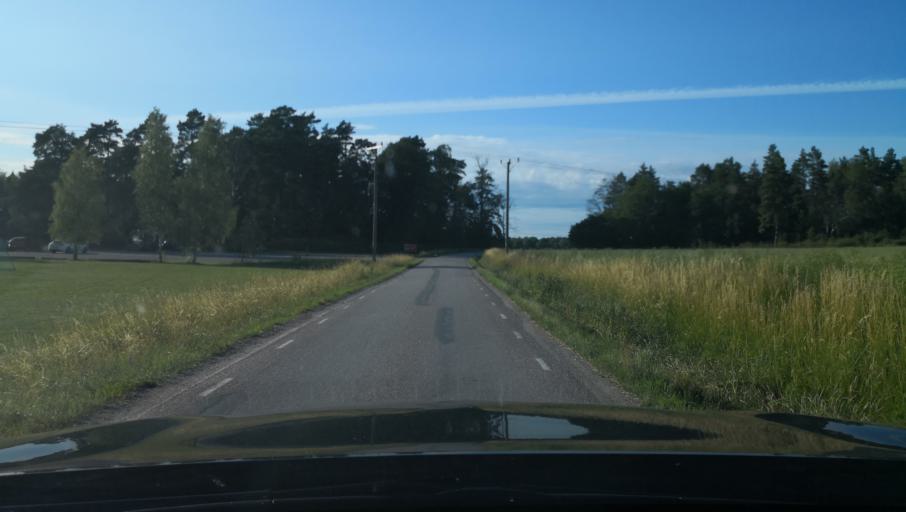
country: SE
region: Uppsala
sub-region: Uppsala Kommun
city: Vattholma
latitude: 59.9188
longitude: 17.8414
